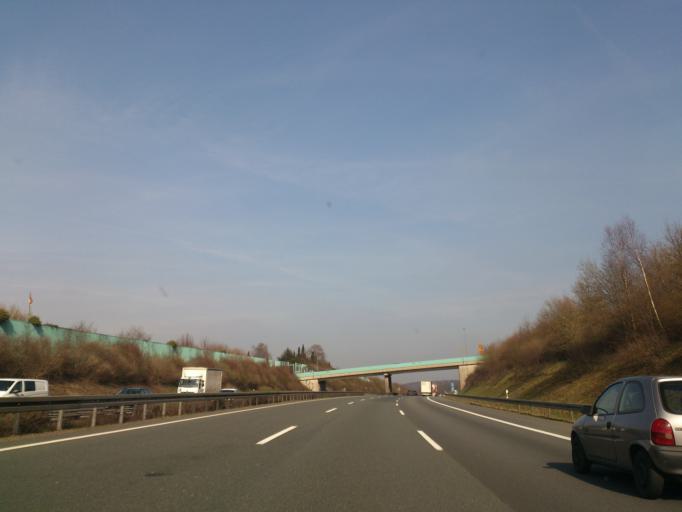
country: DE
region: North Rhine-Westphalia
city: Wetter (Ruhr)
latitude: 51.3583
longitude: 7.3739
